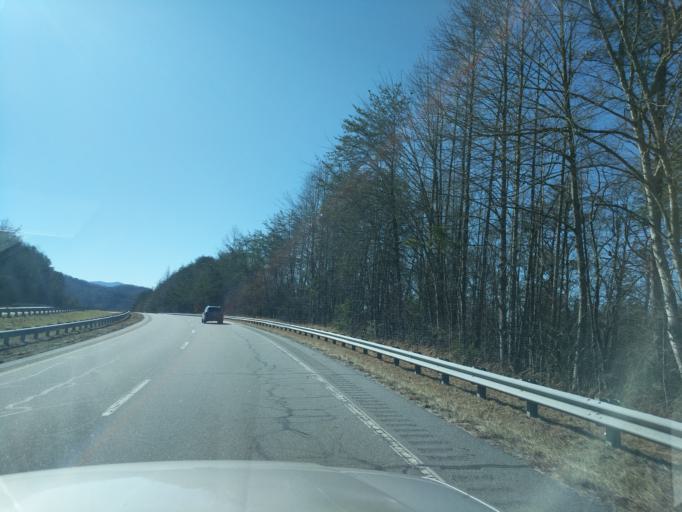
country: US
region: North Carolina
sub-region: Swain County
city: Bryson City
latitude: 35.4034
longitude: -83.4694
